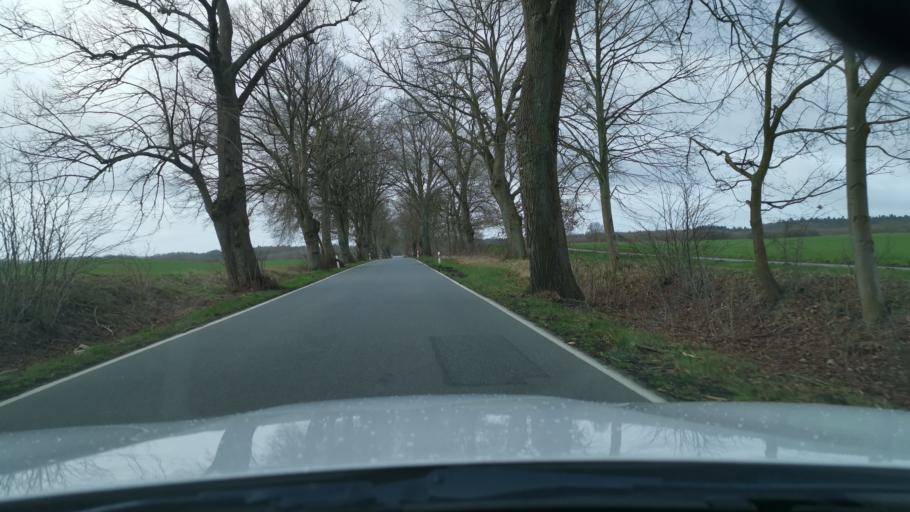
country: DE
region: Mecklenburg-Vorpommern
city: Tessin
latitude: 54.0063
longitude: 12.3990
